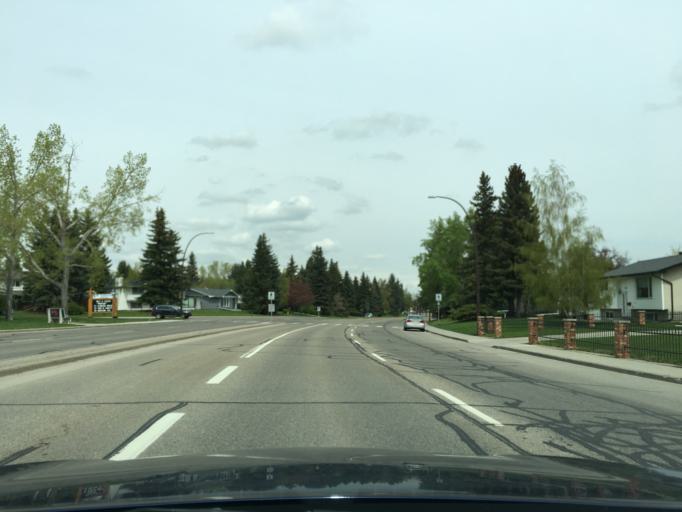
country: CA
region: Alberta
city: Calgary
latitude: 50.9436
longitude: -114.0858
